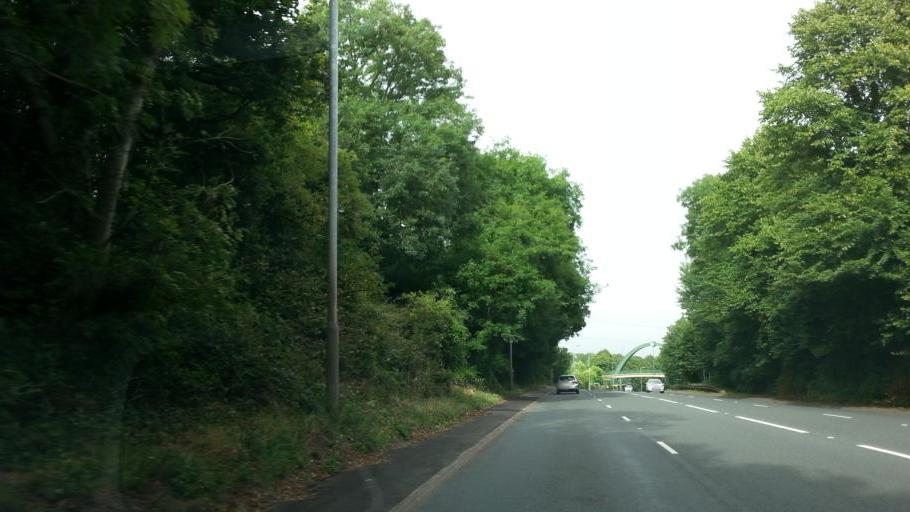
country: GB
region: Wales
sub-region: Newport
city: Marshfield
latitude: 51.5537
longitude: -3.0541
